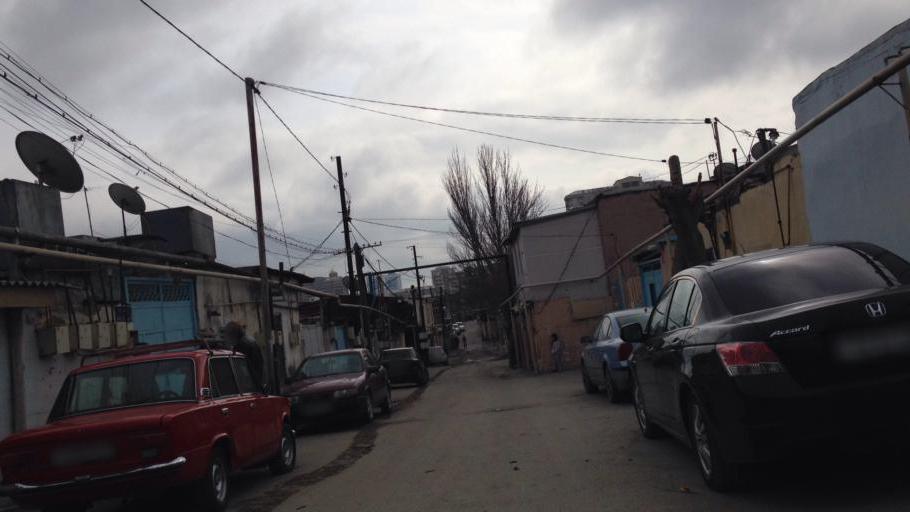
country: AZ
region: Baki
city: Bilajari
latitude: 40.4016
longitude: 49.8273
